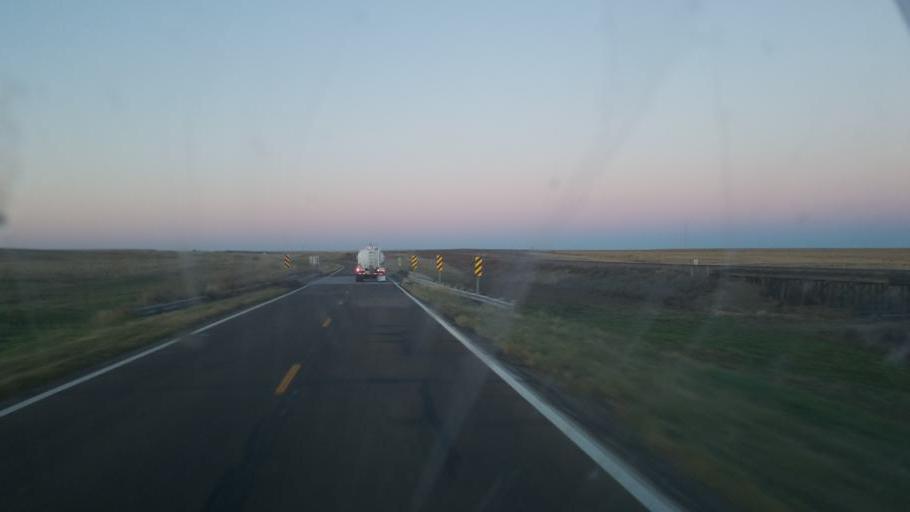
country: US
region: Kansas
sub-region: Wallace County
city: Sharon Springs
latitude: 38.9256
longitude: -101.5599
